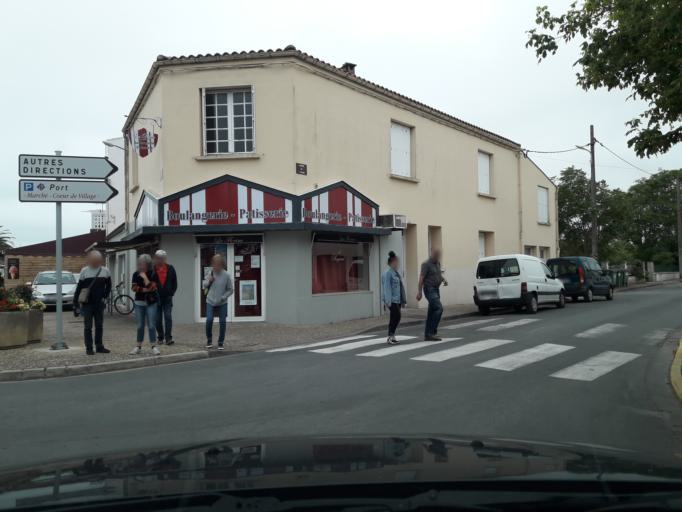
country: FR
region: Poitou-Charentes
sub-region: Departement de la Charente-Maritime
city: Boyard-Ville
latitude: 45.9670
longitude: -1.2432
